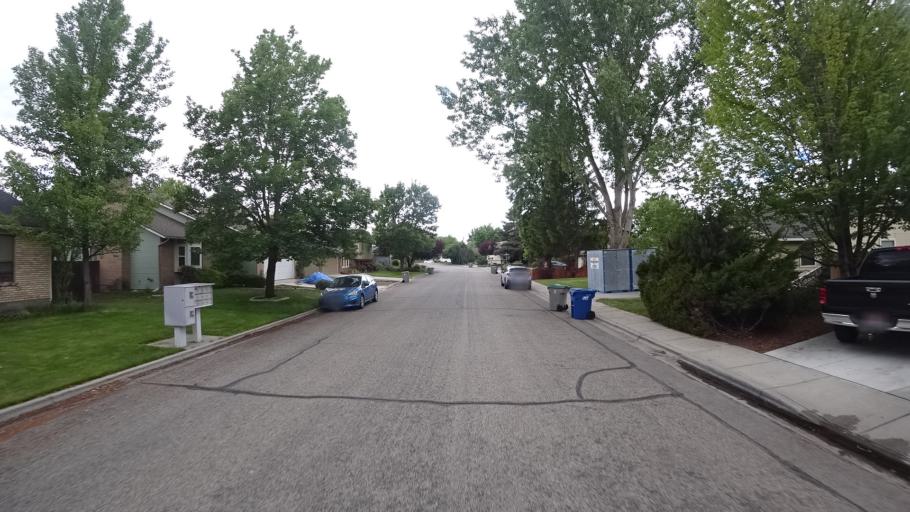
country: US
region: Idaho
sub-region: Ada County
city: Garden City
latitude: 43.6691
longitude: -116.2563
